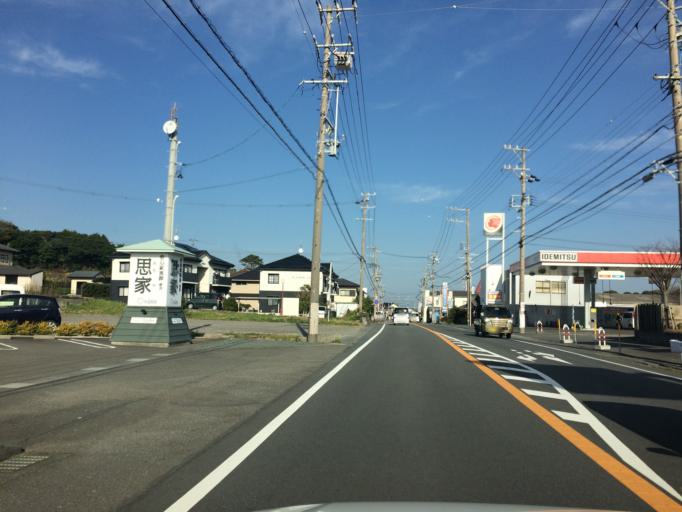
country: JP
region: Shizuoka
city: Oyama
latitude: 34.6315
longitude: 138.1873
